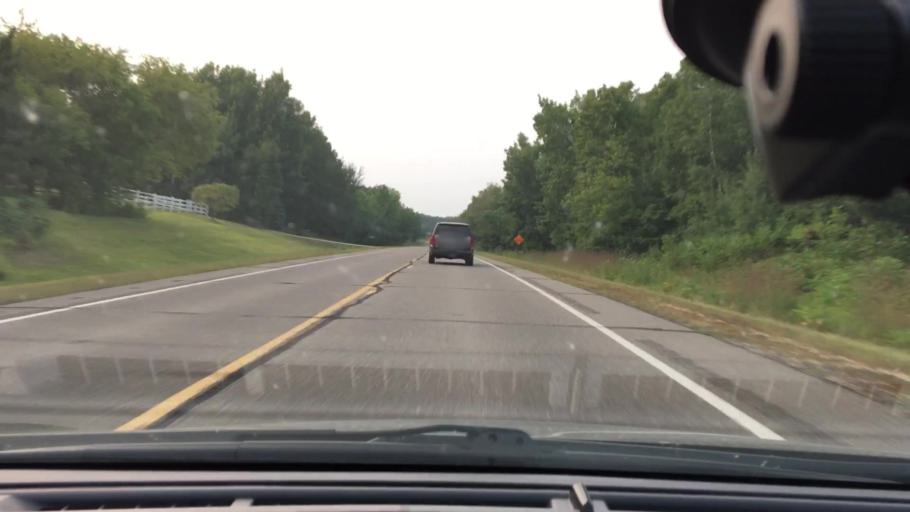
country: US
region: Minnesota
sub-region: Crow Wing County
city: Crosby
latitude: 46.4366
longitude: -93.8743
